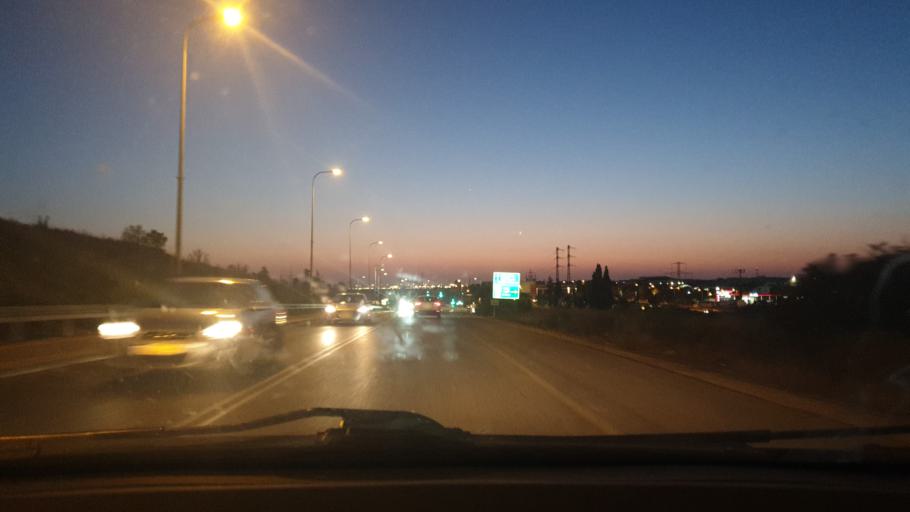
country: IL
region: Central District
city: Bene 'Ayish
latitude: 31.7951
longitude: 34.7636
